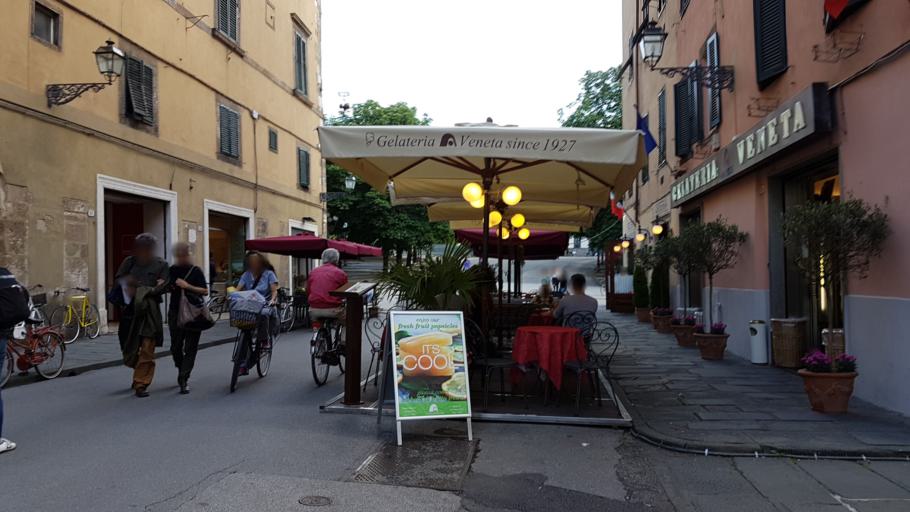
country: IT
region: Tuscany
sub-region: Provincia di Lucca
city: Lucca
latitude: 43.8401
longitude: 10.5017
